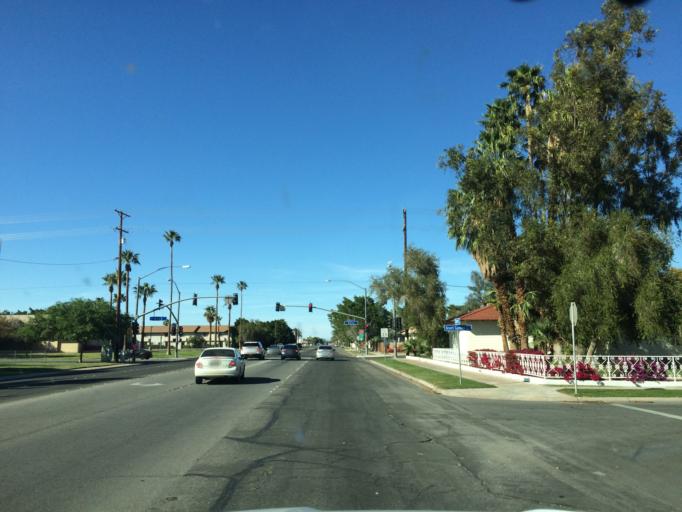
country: US
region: California
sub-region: Imperial County
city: El Centro
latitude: 32.7808
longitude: -115.5612
